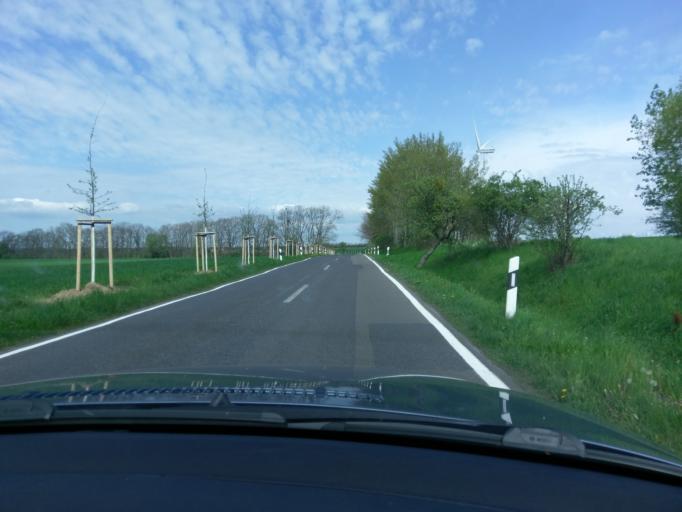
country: DE
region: Brandenburg
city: Eberswalde
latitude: 52.7460
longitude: 13.8540
